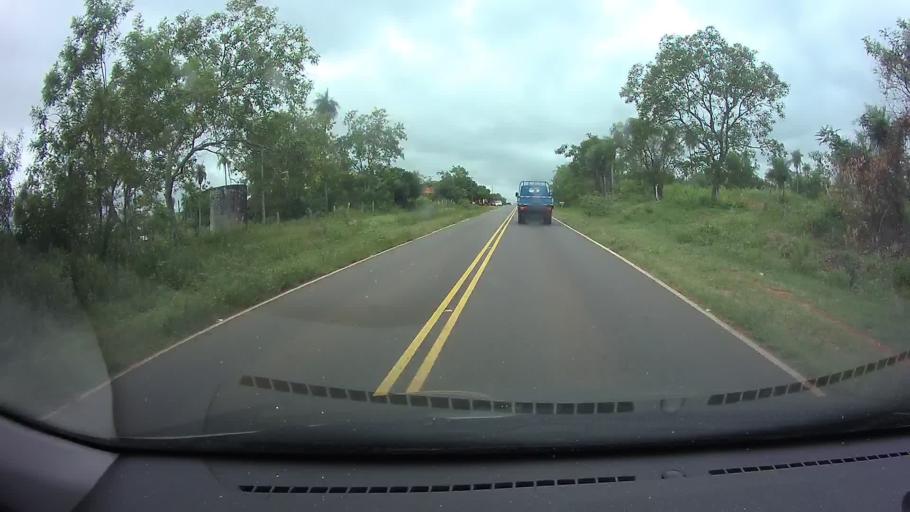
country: PY
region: Paraguari
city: Carapegua
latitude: -25.7256
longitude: -57.3185
